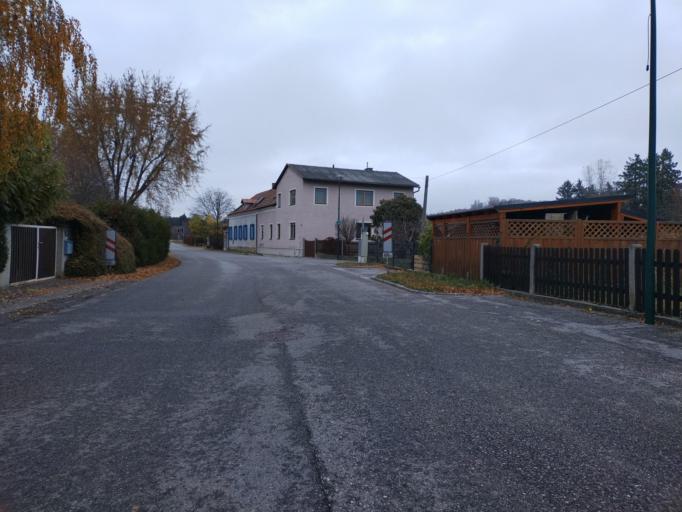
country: AT
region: Lower Austria
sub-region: Politischer Bezirk Neunkirchen
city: Pitten
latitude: 47.7219
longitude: 16.1906
